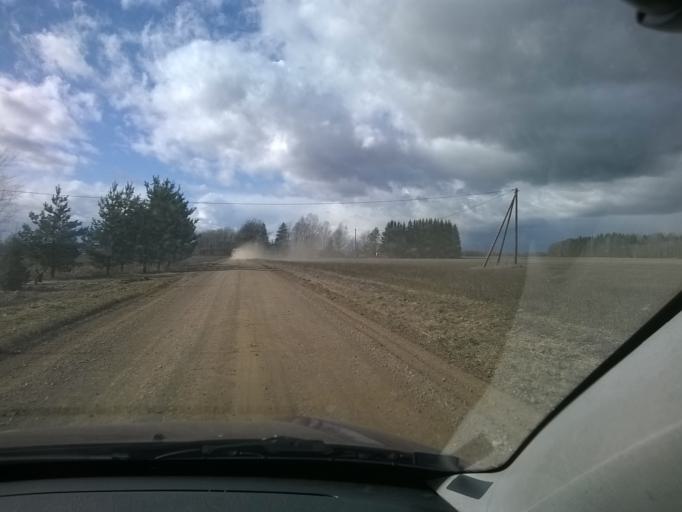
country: EE
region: Tartu
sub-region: Alatskivi vald
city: Kallaste
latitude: 58.3822
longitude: 27.0676
